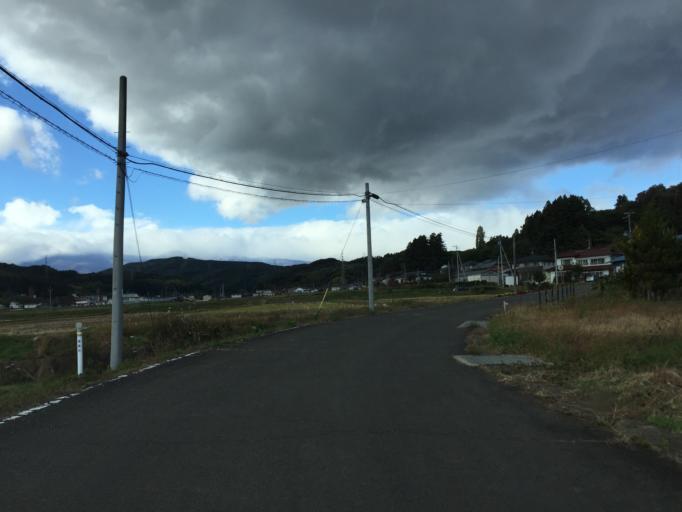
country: JP
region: Fukushima
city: Nihommatsu
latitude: 37.6636
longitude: 140.4304
